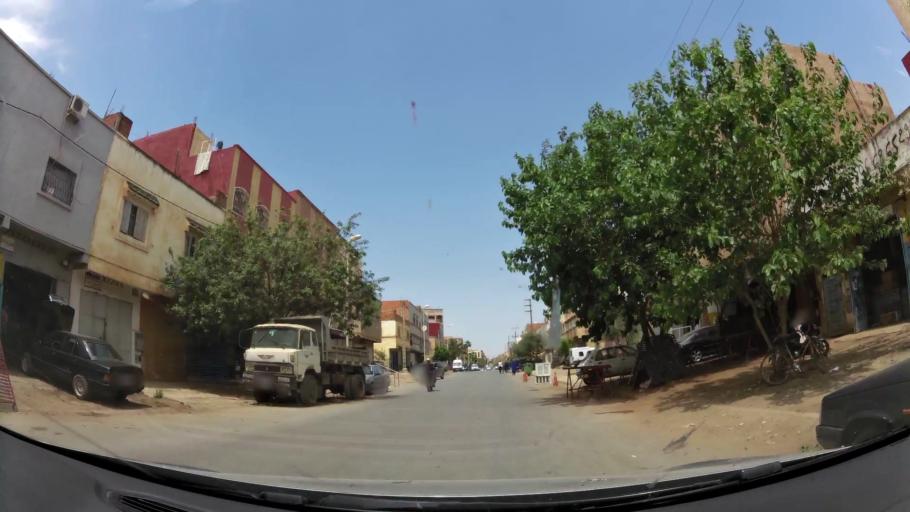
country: MA
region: Rabat-Sale-Zemmour-Zaer
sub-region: Khemisset
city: Khemisset
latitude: 33.8224
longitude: -6.0770
